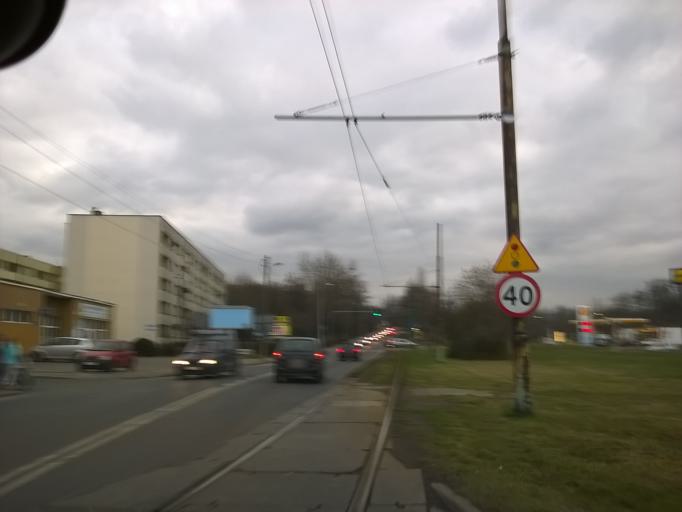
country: PL
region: Silesian Voivodeship
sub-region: Swietochlowice
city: Swietochlowice
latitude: 50.2824
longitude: 18.9133
